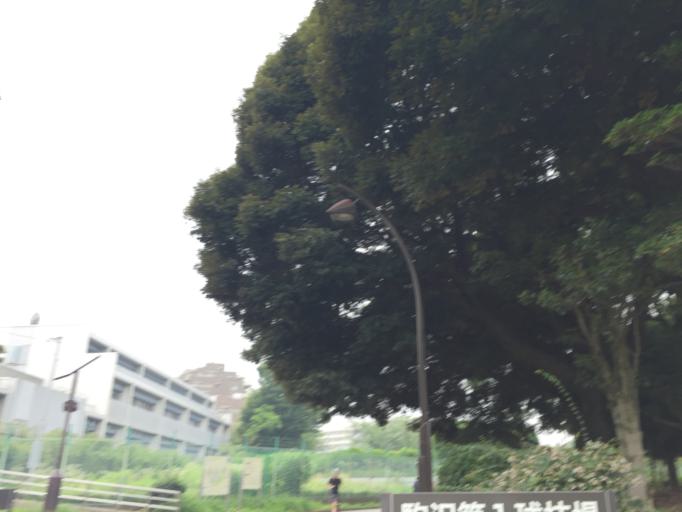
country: JP
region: Tokyo
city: Tokyo
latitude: 35.6218
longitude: 139.6627
